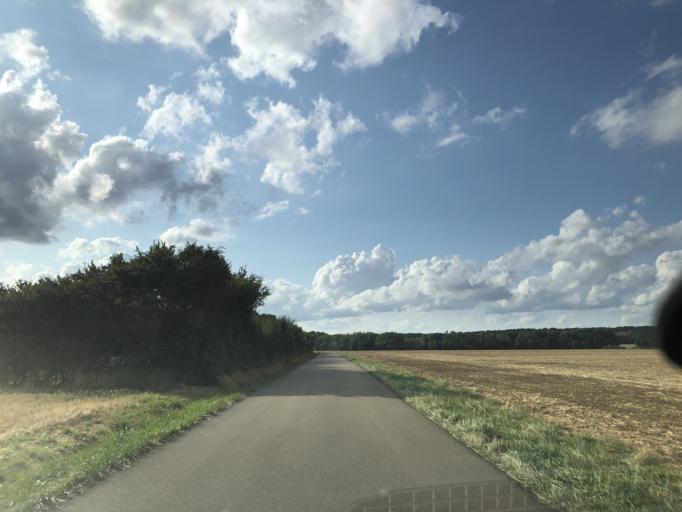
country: FR
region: Bourgogne
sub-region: Departement de l'Yonne
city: Charbuy
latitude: 47.8214
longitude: 3.4909
